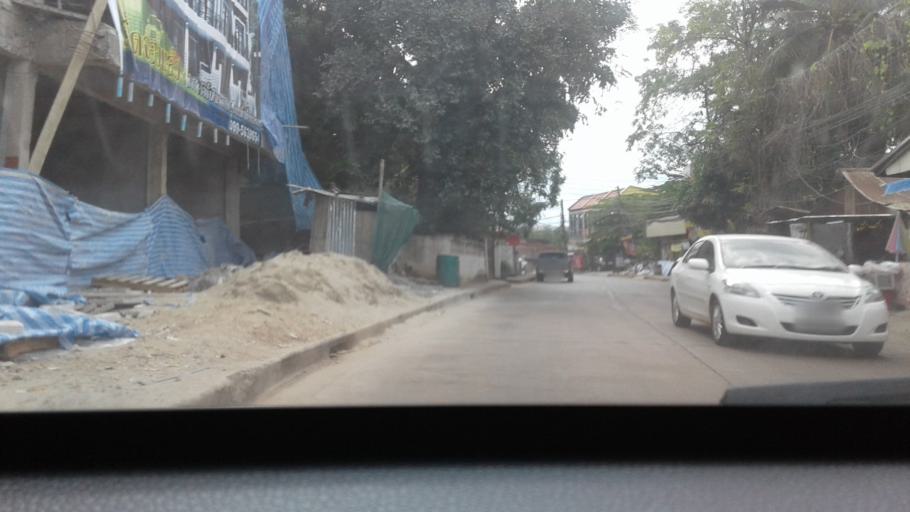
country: TH
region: Changwat Udon Thani
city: Udon Thani
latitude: 17.4252
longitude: 102.7835
